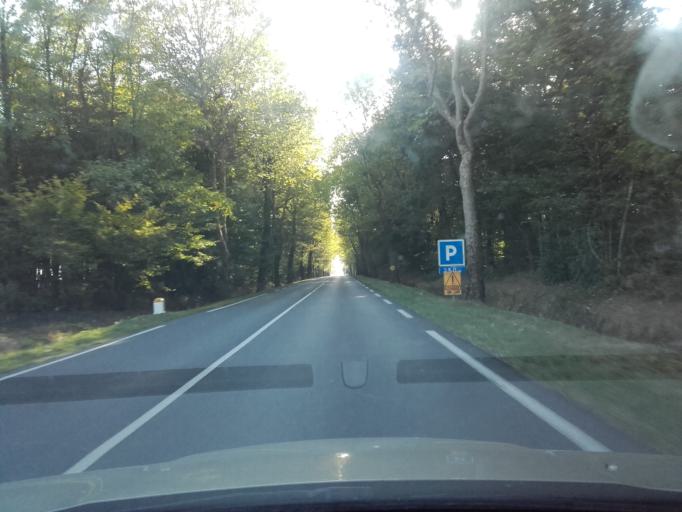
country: FR
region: Centre
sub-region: Departement d'Indre-et-Loire
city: Monnaie
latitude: 47.4898
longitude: 0.7747
